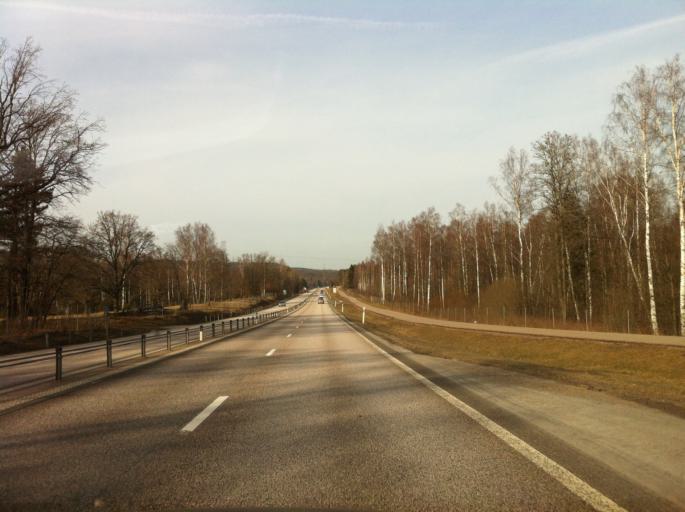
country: SE
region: Vaestra Goetaland
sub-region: Skovde Kommun
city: Stopen
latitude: 58.4354
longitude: 13.8592
